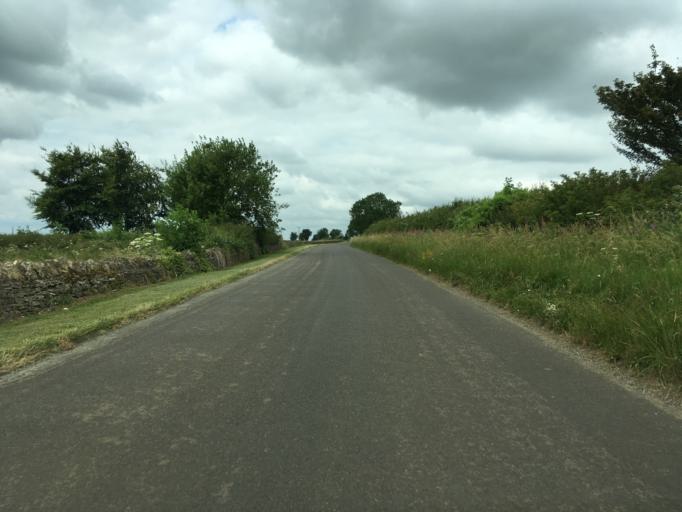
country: GB
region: England
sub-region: Oxfordshire
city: Chipping Norton
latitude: 51.9239
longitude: -1.5494
